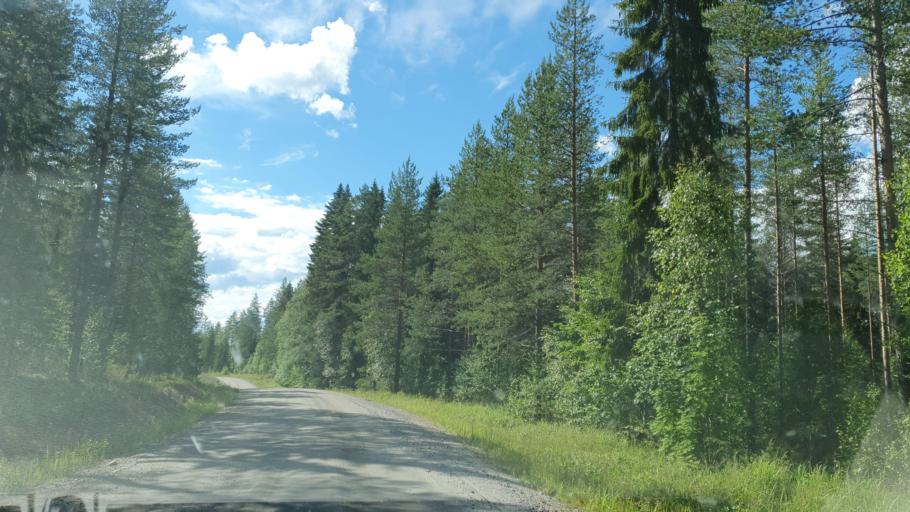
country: FI
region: Kainuu
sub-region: Kehys-Kainuu
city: Kuhmo
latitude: 64.1513
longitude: 29.7347
